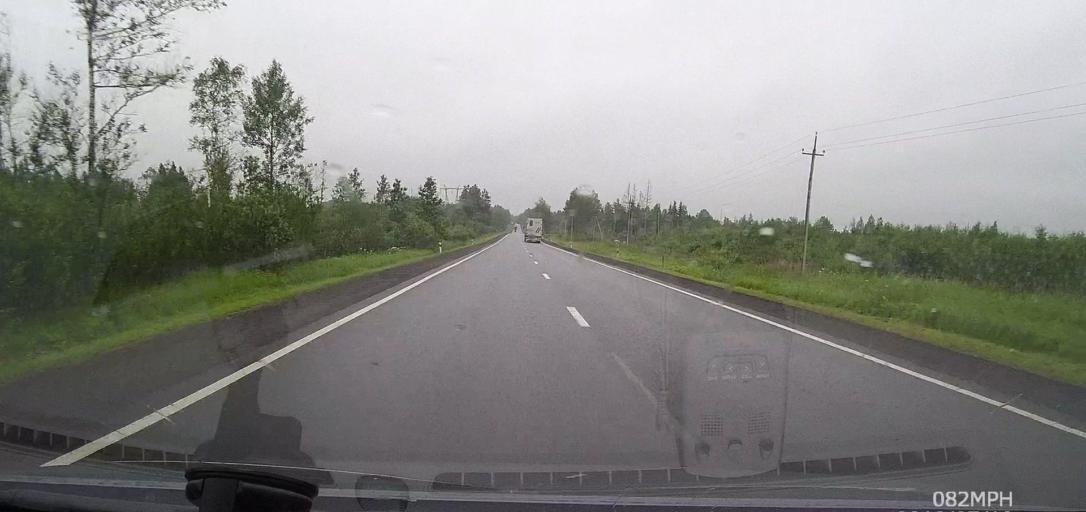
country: RU
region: Leningrad
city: Staraya Ladoga
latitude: 60.0292
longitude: 32.2081
